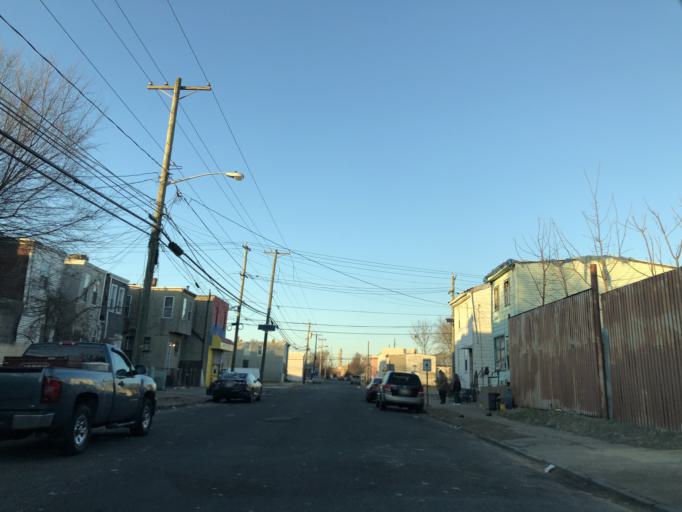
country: US
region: New Jersey
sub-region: Camden County
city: Camden
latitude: 39.9319
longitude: -75.1177
